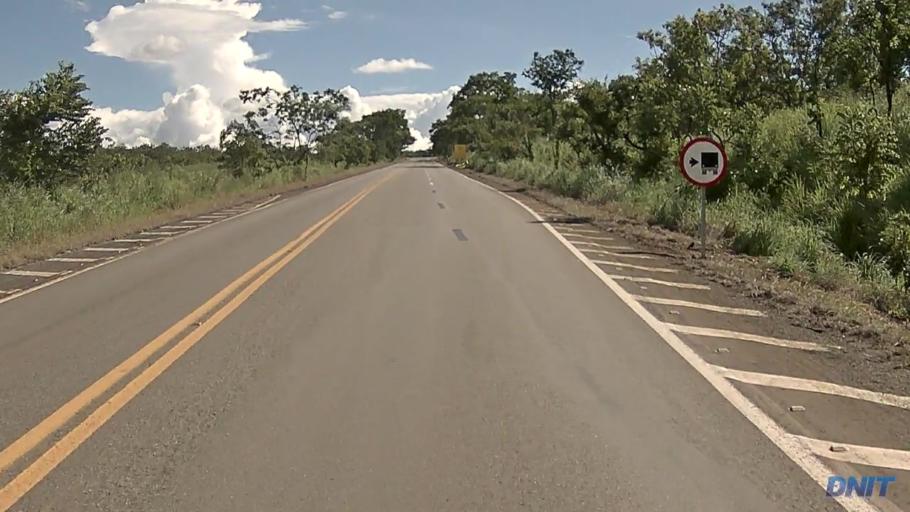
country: BR
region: Goias
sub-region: Padre Bernardo
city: Padre Bernardo
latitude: -15.1884
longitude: -48.4344
